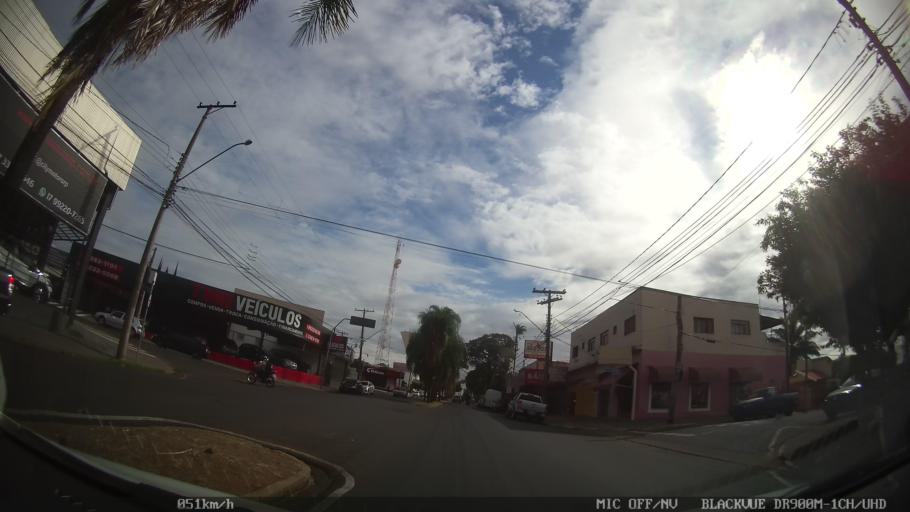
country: BR
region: Sao Paulo
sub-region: Sao Jose Do Rio Preto
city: Sao Jose do Rio Preto
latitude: -20.8312
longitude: -49.3721
